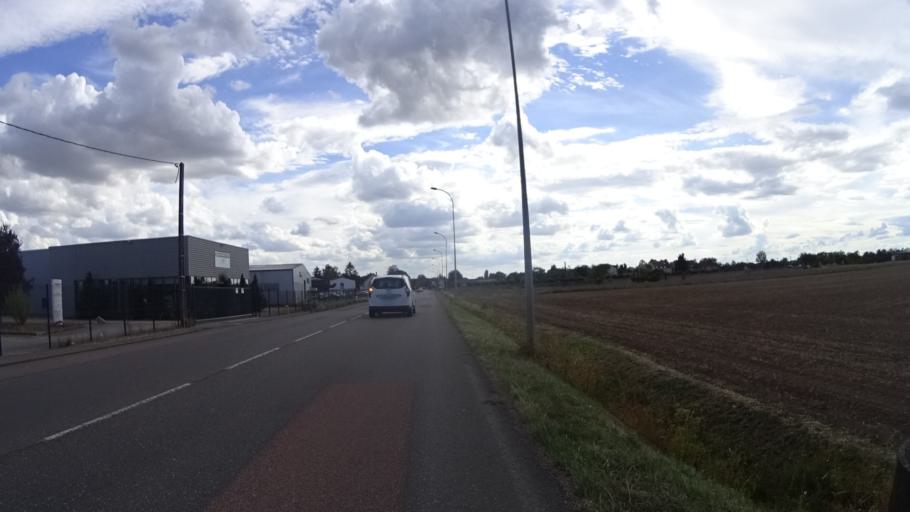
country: FR
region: Bourgogne
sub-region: Departement de la Cote-d'Or
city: Seurre
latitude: 47.0072
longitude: 5.1534
